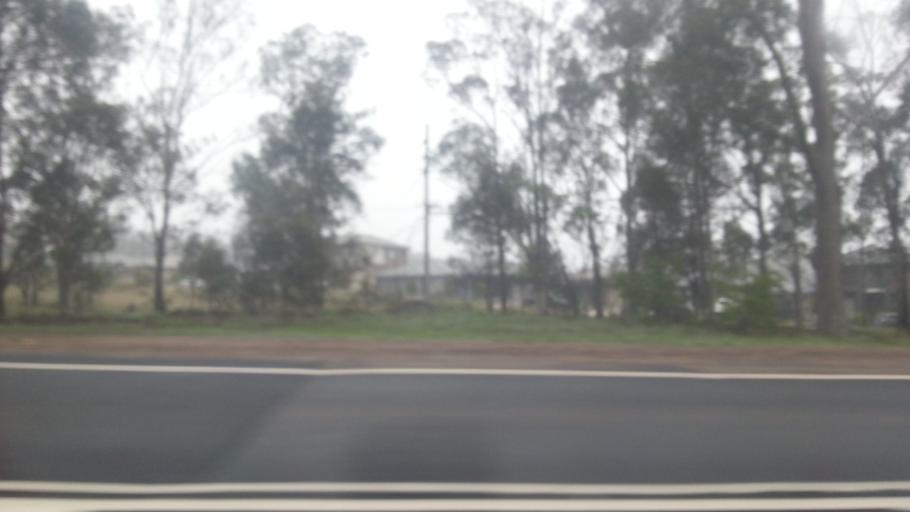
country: AU
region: New South Wales
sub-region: Penrith Municipality
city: Werrington Downs
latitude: -33.7160
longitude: 150.7260
